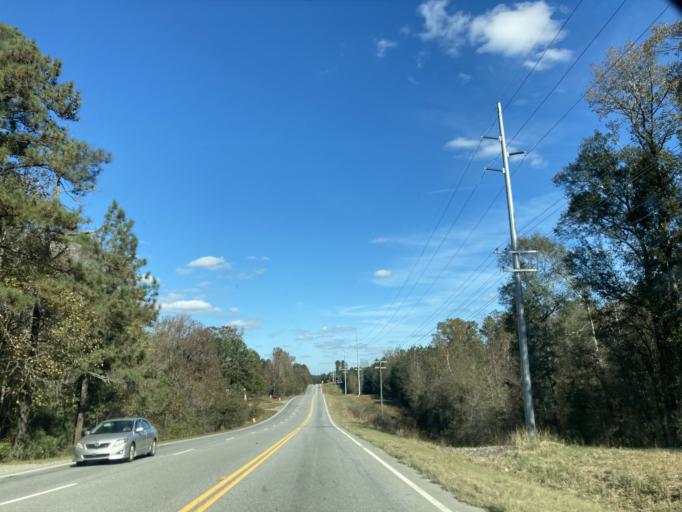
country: US
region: Georgia
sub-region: Jones County
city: Gray
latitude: 32.9241
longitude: -83.5088
